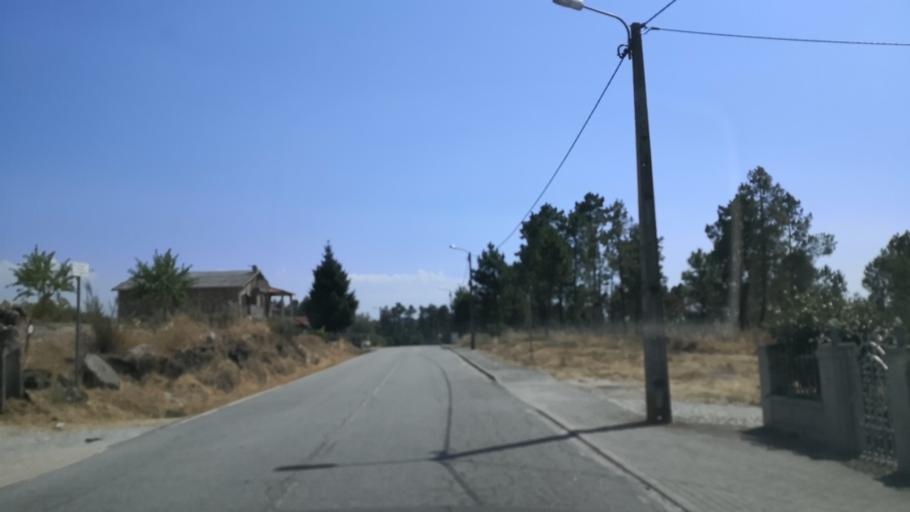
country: PT
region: Vila Real
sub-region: Murca
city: Murca
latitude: 41.3645
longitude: -7.4917
